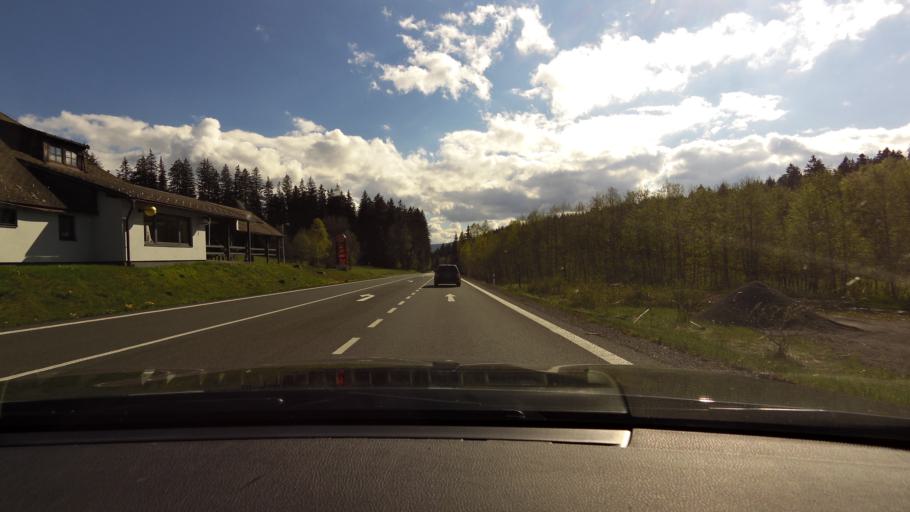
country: CZ
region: Plzensky
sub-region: Okres Klatovy
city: Zelezna Ruda
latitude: 49.1495
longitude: 13.2560
